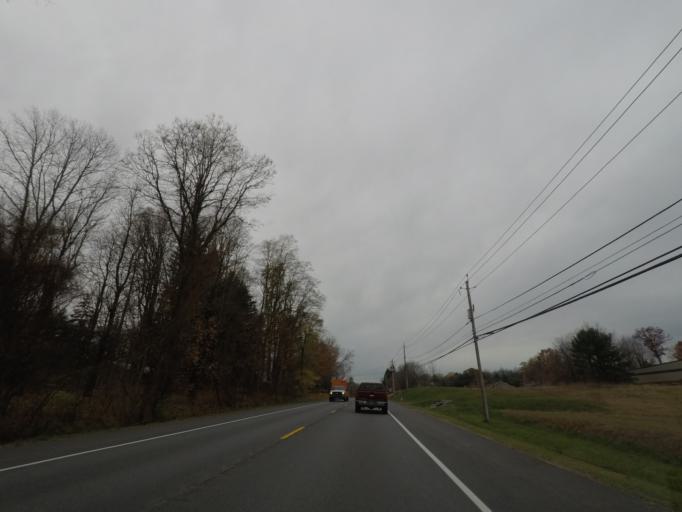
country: US
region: New York
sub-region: Saratoga County
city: Mechanicville
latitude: 42.8645
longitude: -73.7482
